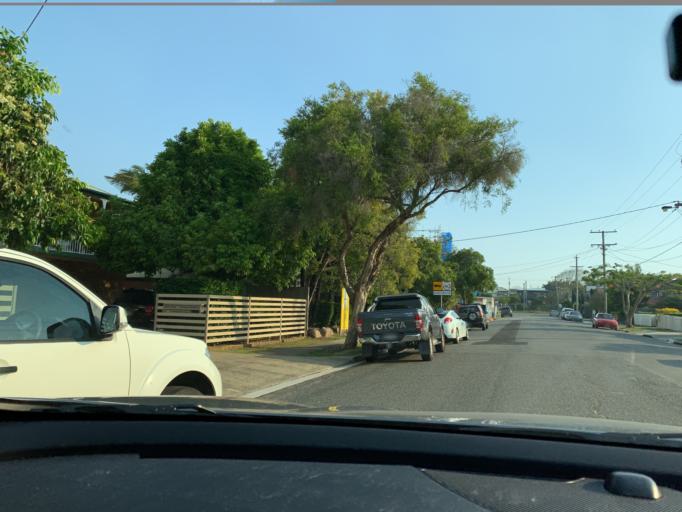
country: AU
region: Queensland
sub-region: Brisbane
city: Ascot
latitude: -27.4298
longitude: 153.0772
